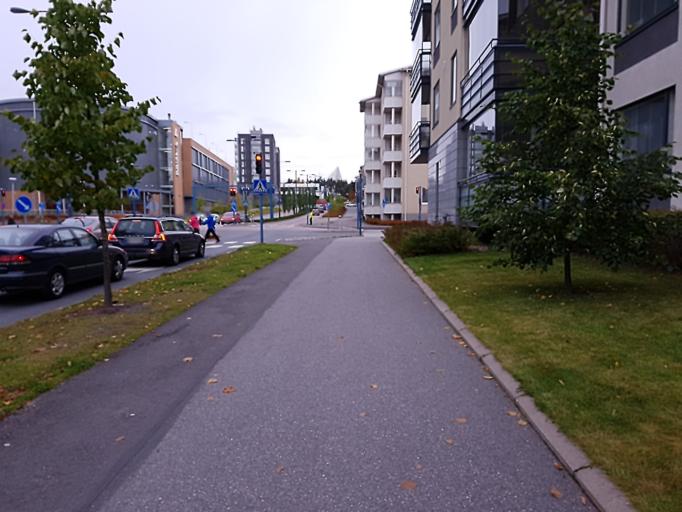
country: FI
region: Uusimaa
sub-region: Helsinki
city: Hyvinge
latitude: 60.6302
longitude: 24.8696
